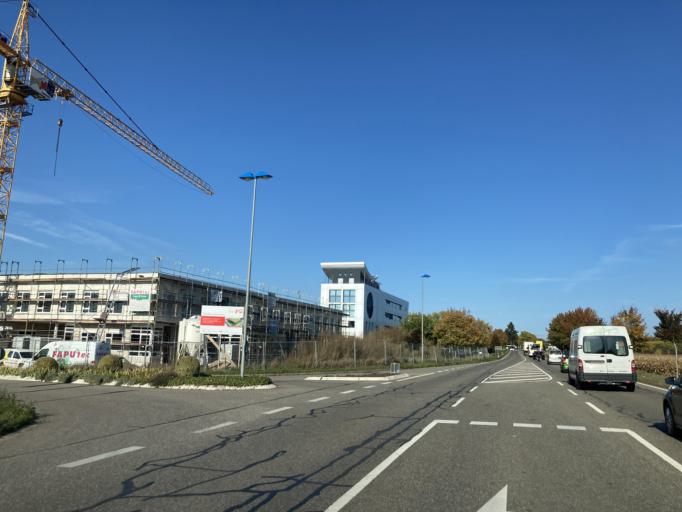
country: DE
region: Baden-Wuerttemberg
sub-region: Freiburg Region
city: Heitersheim
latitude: 47.8690
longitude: 7.6483
